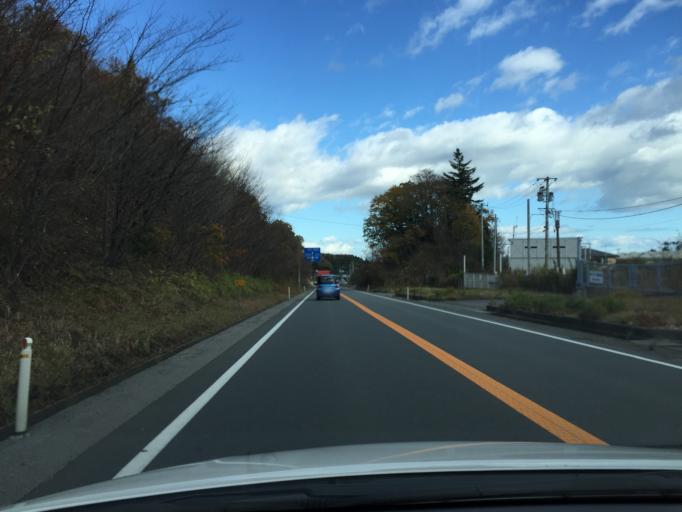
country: JP
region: Fukushima
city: Namie
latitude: 37.4120
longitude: 140.9978
